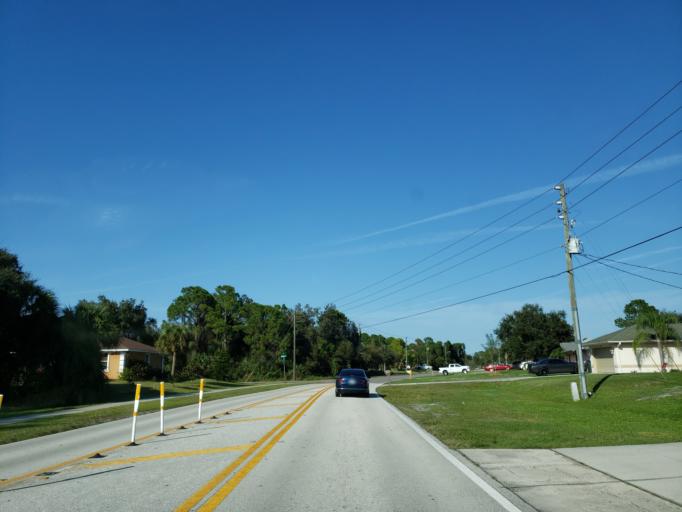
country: US
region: Florida
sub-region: Sarasota County
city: North Port
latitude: 27.0700
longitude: -82.1974
